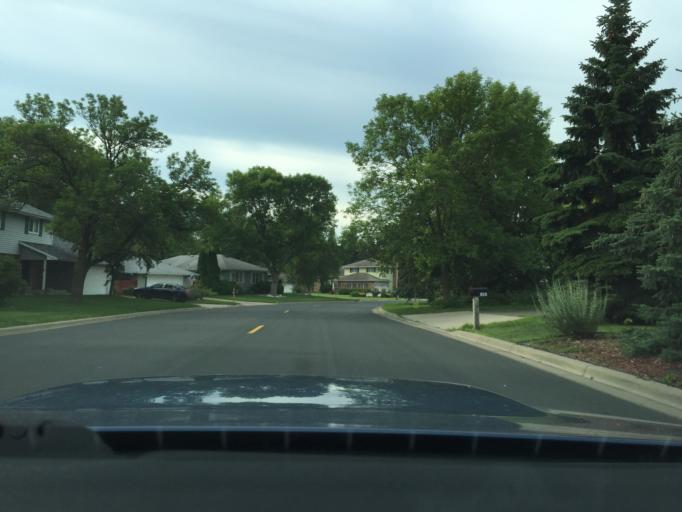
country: US
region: Minnesota
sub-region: Dakota County
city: West Saint Paul
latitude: 44.9015
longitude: -93.1015
